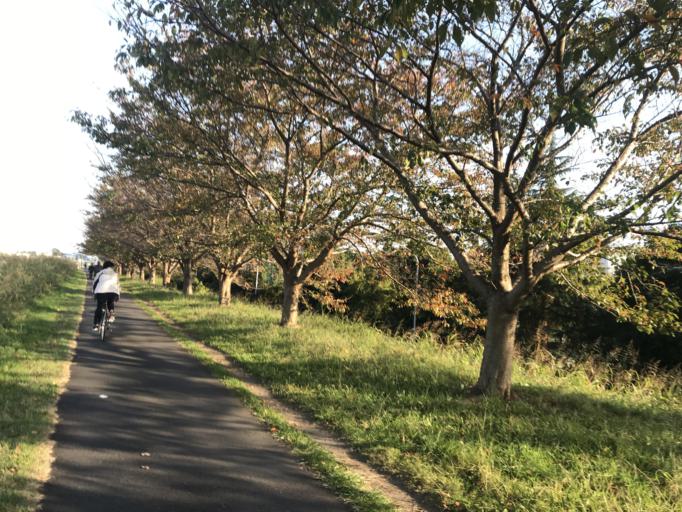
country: JP
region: Kanagawa
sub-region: Kawasaki-shi
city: Kawasaki
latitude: 35.5887
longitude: 139.6558
